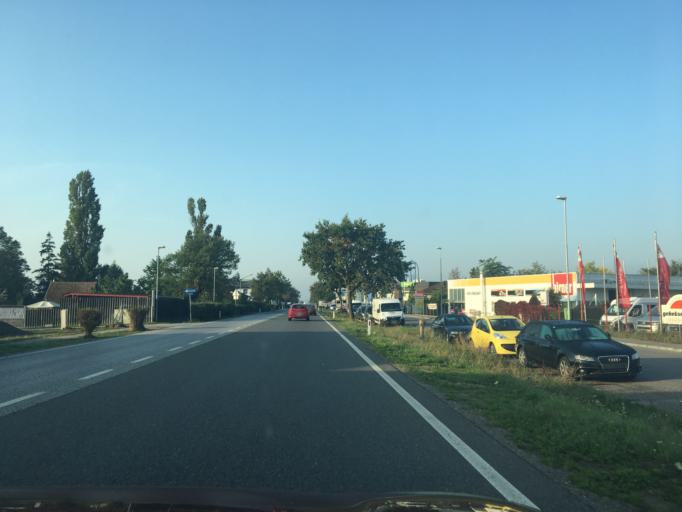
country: AT
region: Lower Austria
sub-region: Politischer Bezirk Mistelbach
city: Grossebersdorf
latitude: 48.3352
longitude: 16.4592
